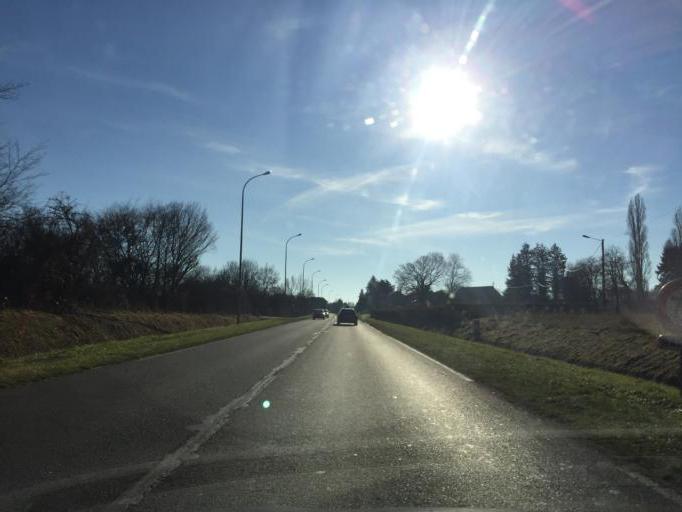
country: FR
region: Auvergne
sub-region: Departement de l'Allier
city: Bellerive-sur-Allier
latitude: 46.1500
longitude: 3.3940
